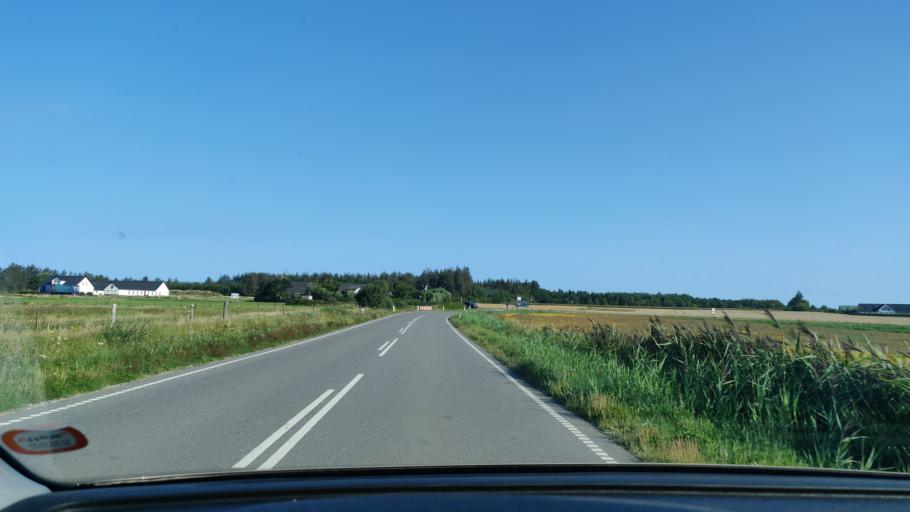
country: DK
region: North Denmark
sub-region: Jammerbugt Kommune
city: Pandrup
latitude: 57.2442
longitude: 9.6468
